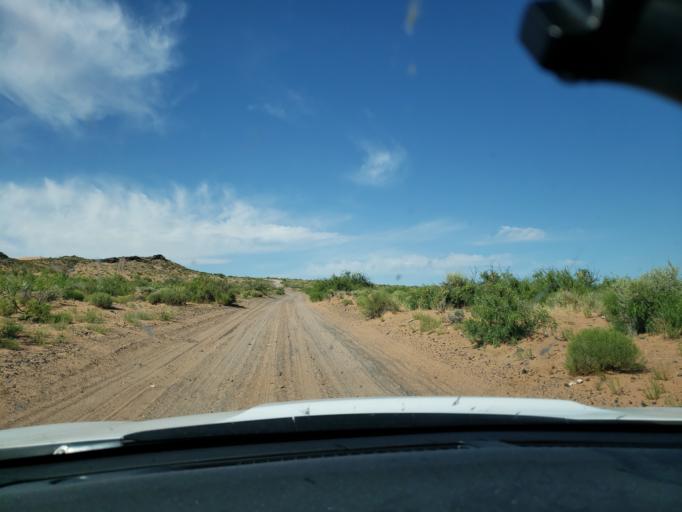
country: US
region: New Mexico
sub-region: Dona Ana County
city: San Miguel
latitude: 32.0811
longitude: -106.7920
